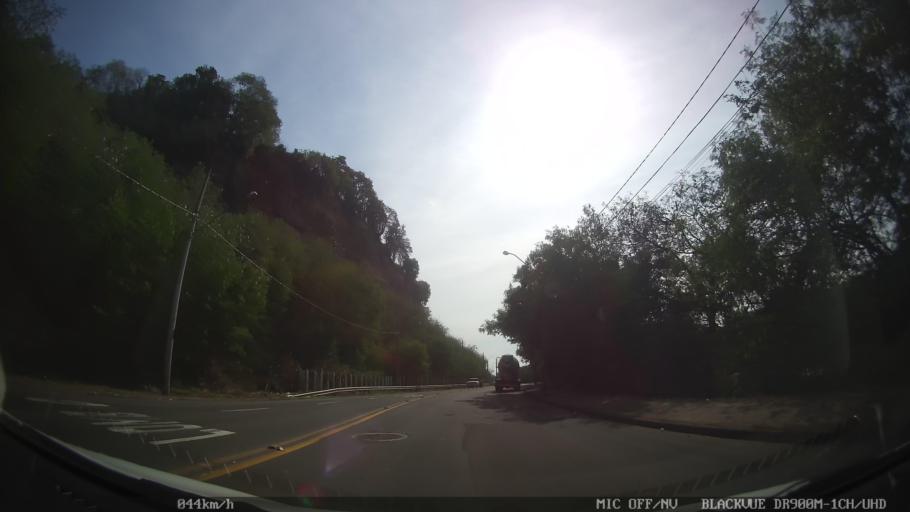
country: BR
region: Sao Paulo
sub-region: Piracicaba
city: Piracicaba
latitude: -22.7148
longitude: -47.6778
